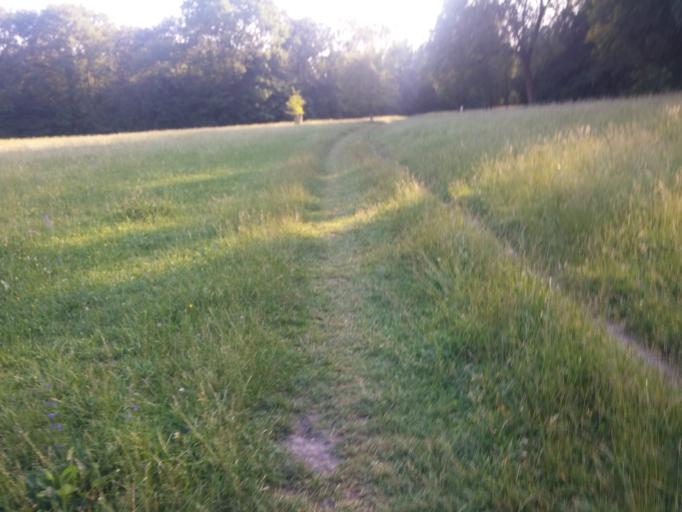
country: DE
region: Bavaria
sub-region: Upper Bavaria
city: Bogenhausen
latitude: 48.1734
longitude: 11.6106
